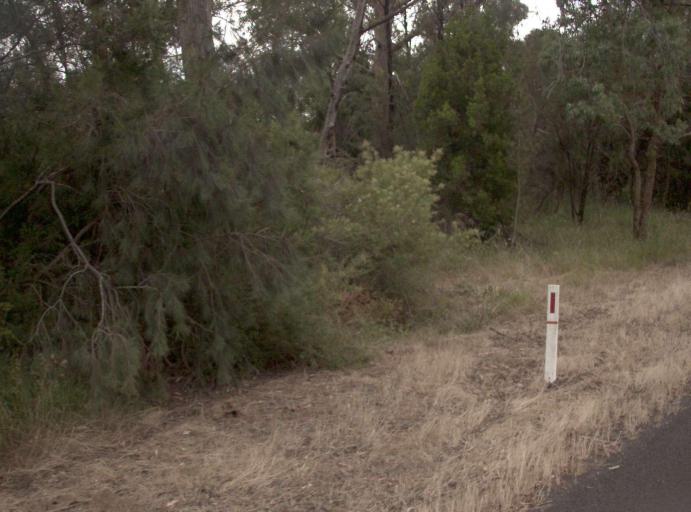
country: AU
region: Victoria
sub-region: Wellington
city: Sale
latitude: -38.3590
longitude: 146.9934
